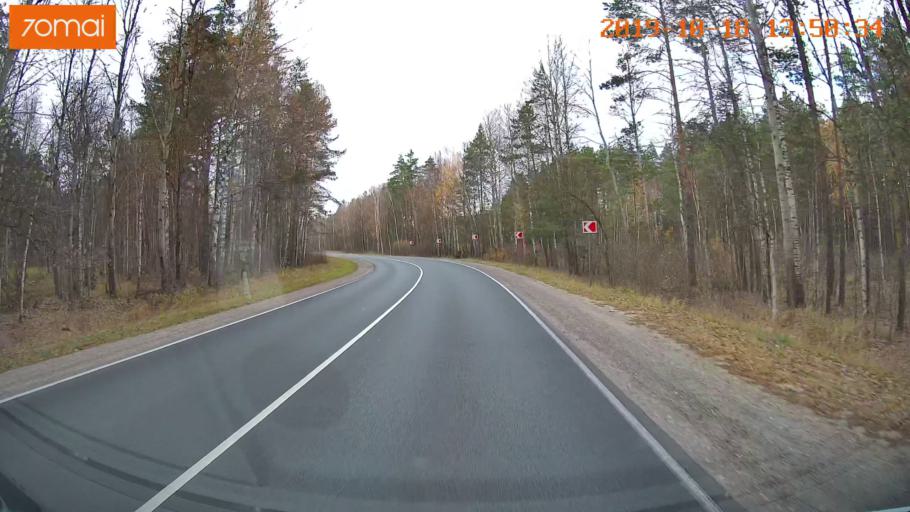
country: RU
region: Moskovskaya
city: Radovitskiy
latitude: 55.0078
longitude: 39.9699
